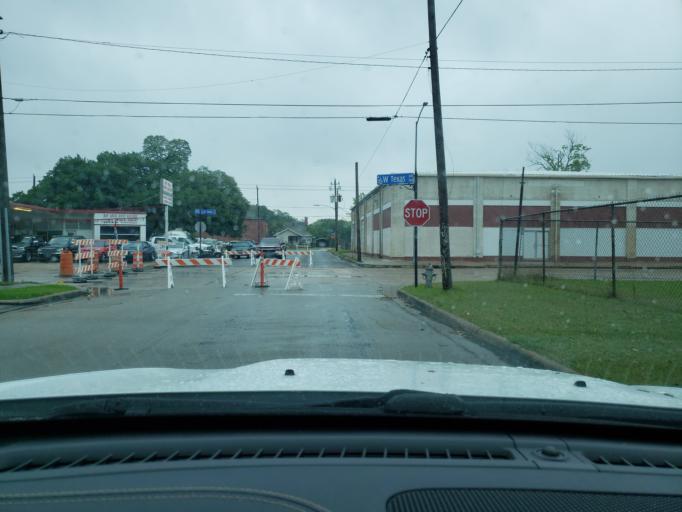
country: US
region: Texas
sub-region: Harris County
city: Baytown
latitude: 29.7339
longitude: -94.9739
